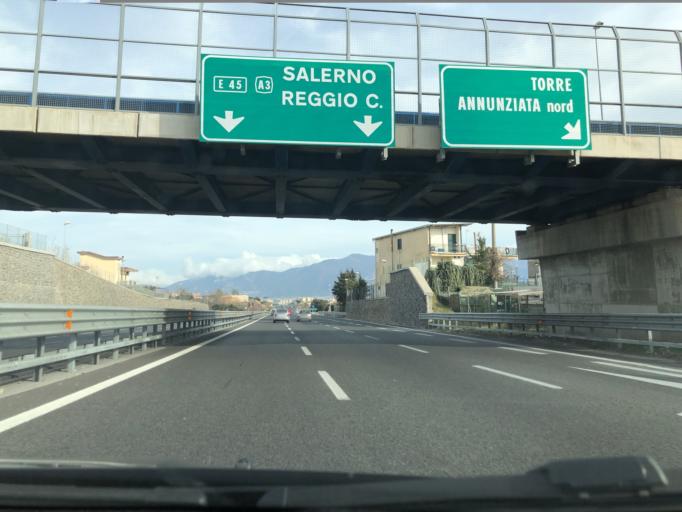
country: IT
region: Campania
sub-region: Provincia di Napoli
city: Trecase
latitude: 40.7677
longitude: 14.4262
